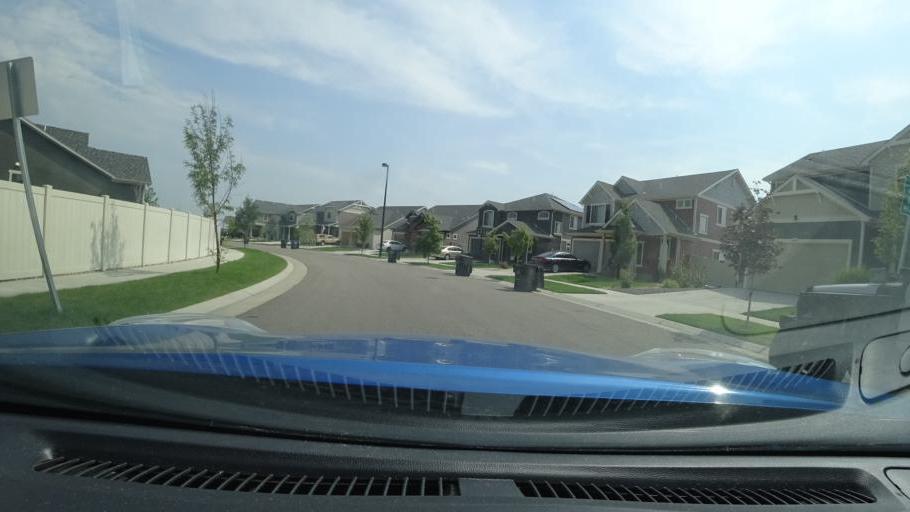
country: US
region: Colorado
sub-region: Adams County
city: Aurora
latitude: 39.7769
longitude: -104.7762
